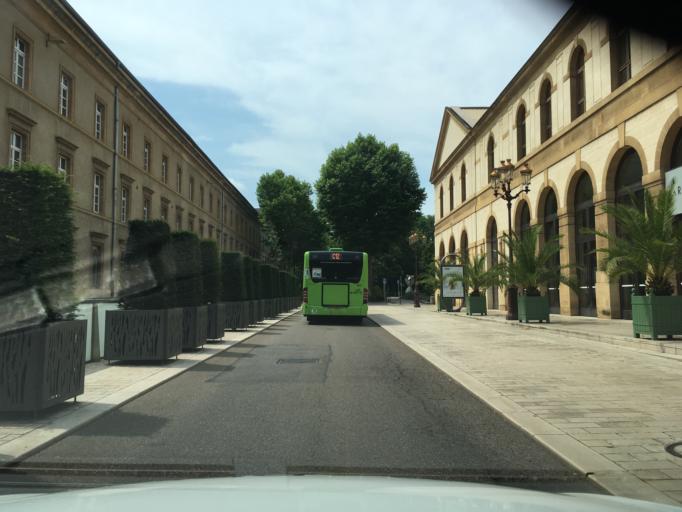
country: FR
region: Lorraine
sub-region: Departement de la Moselle
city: Metz
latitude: 49.1145
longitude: 6.1711
